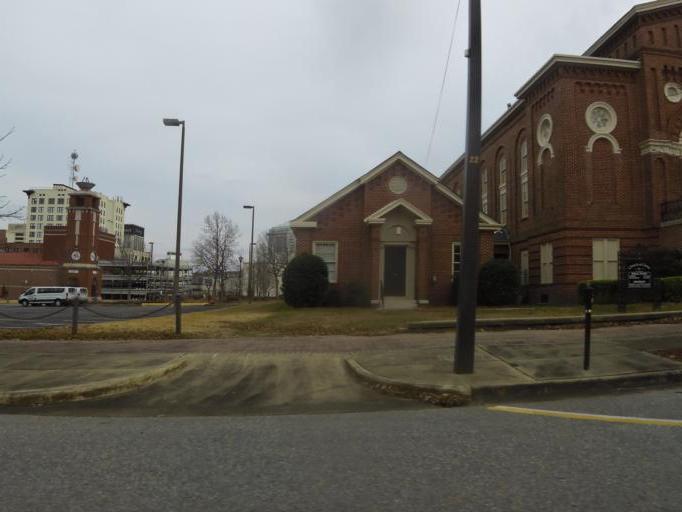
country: US
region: Alabama
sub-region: Montgomery County
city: Montgomery
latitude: 32.3745
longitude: -86.3116
